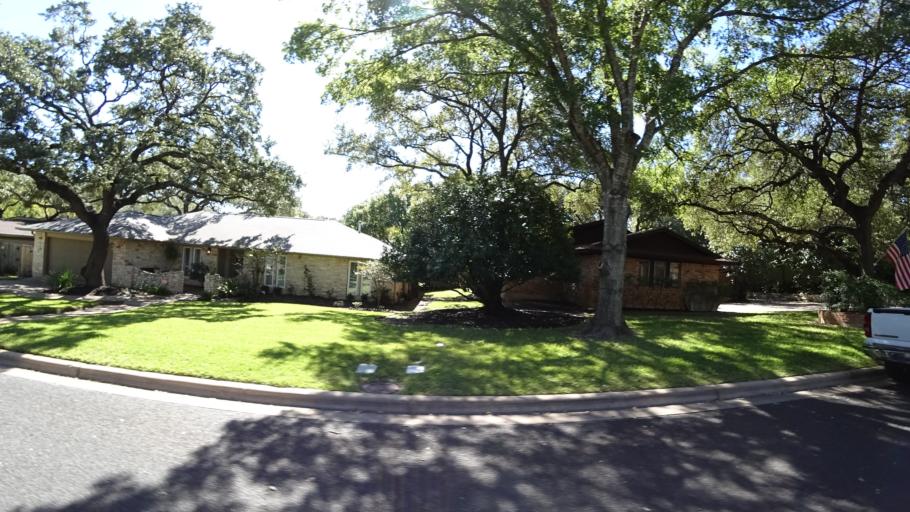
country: US
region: Texas
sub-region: Travis County
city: West Lake Hills
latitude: 30.3644
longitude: -97.7602
